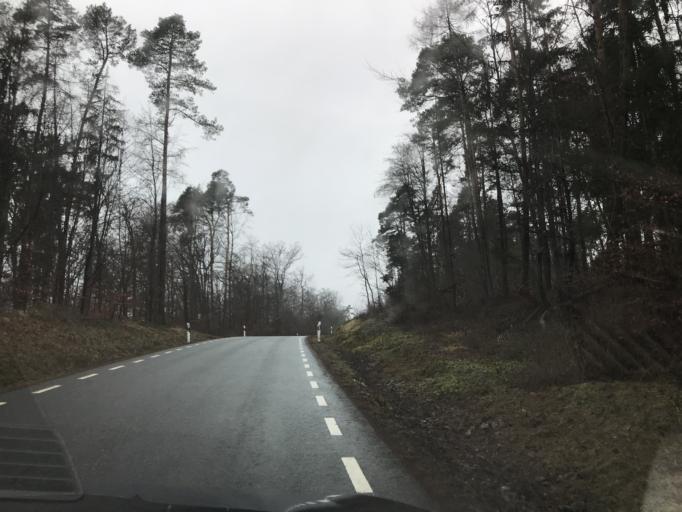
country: DE
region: Baden-Wuerttemberg
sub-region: Regierungsbezirk Stuttgart
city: Weil im Schonbuch
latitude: 48.6116
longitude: 9.0653
